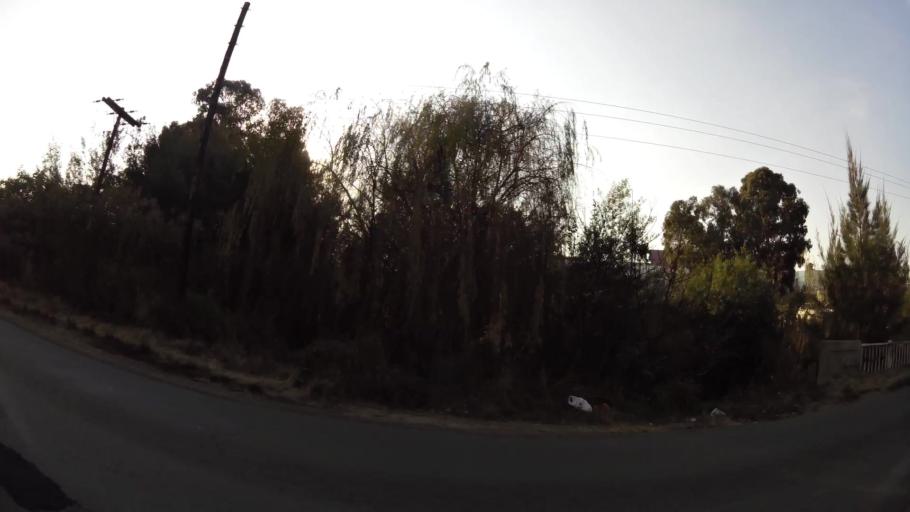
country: ZA
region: Gauteng
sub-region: City of Johannesburg Metropolitan Municipality
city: Midrand
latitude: -26.0307
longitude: 28.1406
